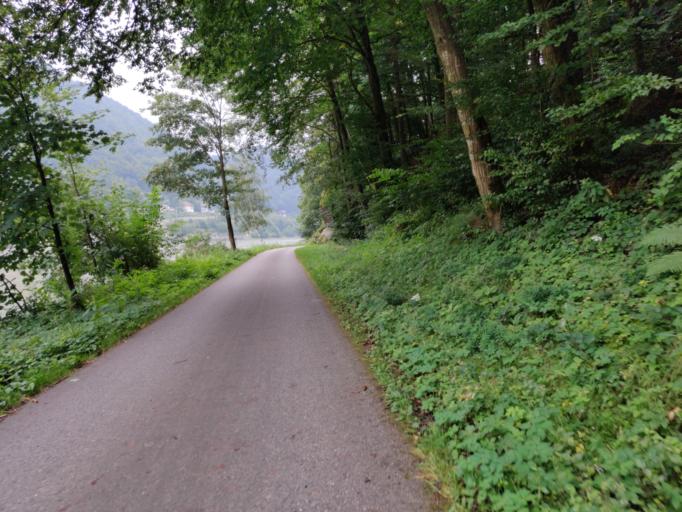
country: AT
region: Lower Austria
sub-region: Politischer Bezirk Melk
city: Nochling
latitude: 48.2306
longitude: 14.9354
